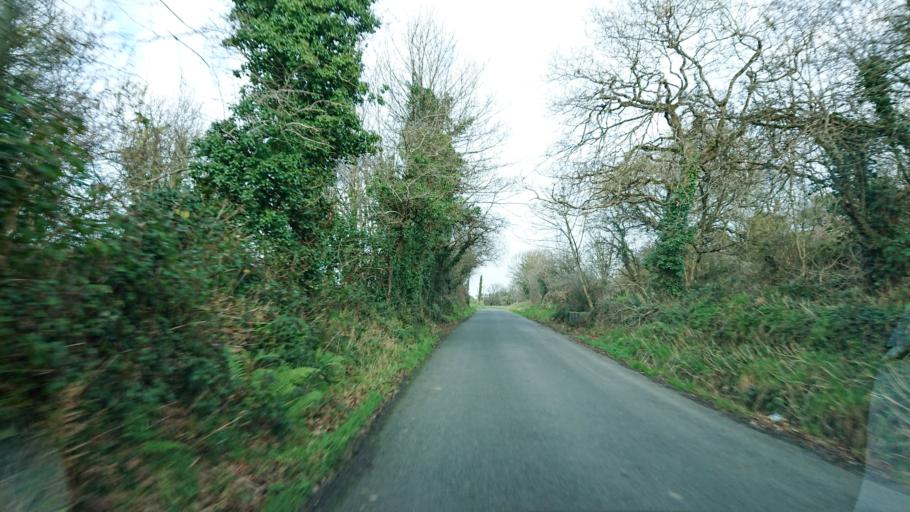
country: IE
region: Munster
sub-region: Waterford
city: Tra Mhor
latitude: 52.1585
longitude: -7.2683
